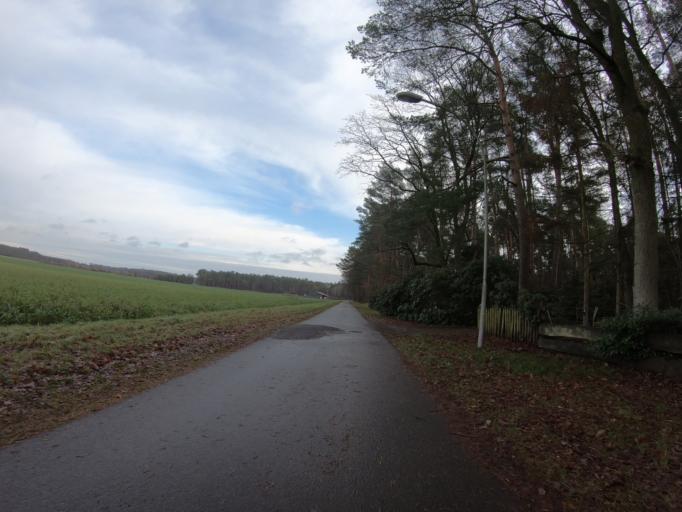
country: DE
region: Lower Saxony
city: Wagenhoff
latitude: 52.4917
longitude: 10.4878
